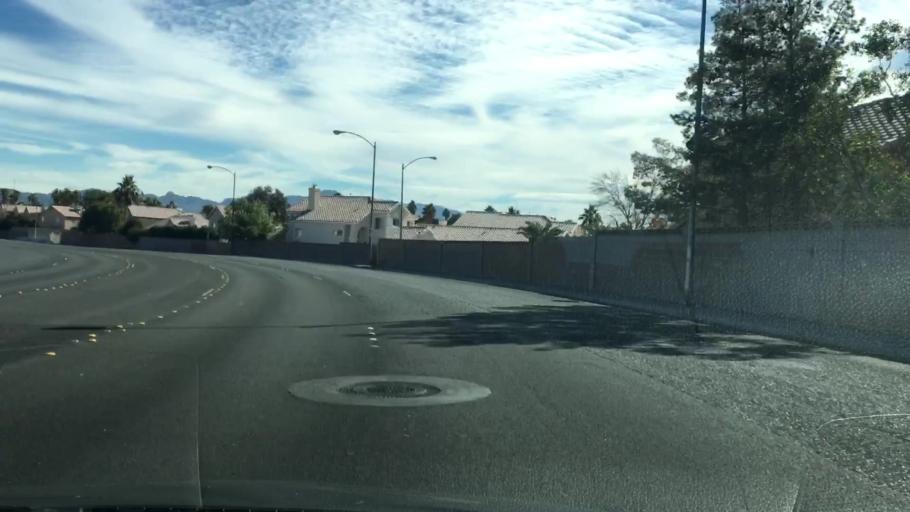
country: US
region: Nevada
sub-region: Clark County
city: Paradise
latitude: 36.0463
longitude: -115.1406
